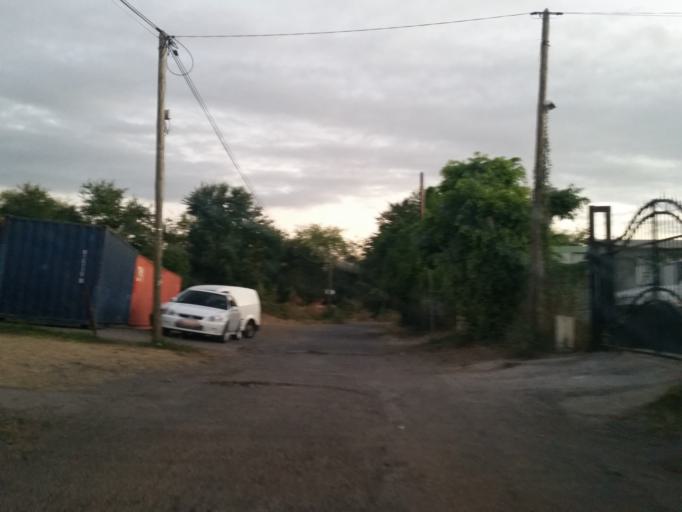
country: RE
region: Reunion
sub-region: Reunion
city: Saint-Paul
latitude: -20.9793
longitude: 55.2963
